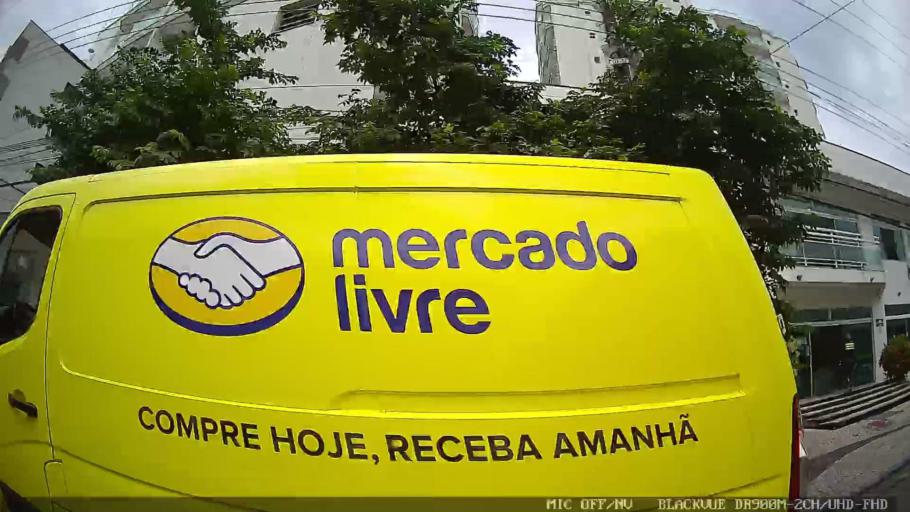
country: BR
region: Sao Paulo
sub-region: Caraguatatuba
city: Caraguatatuba
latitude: -23.6250
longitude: -45.4125
